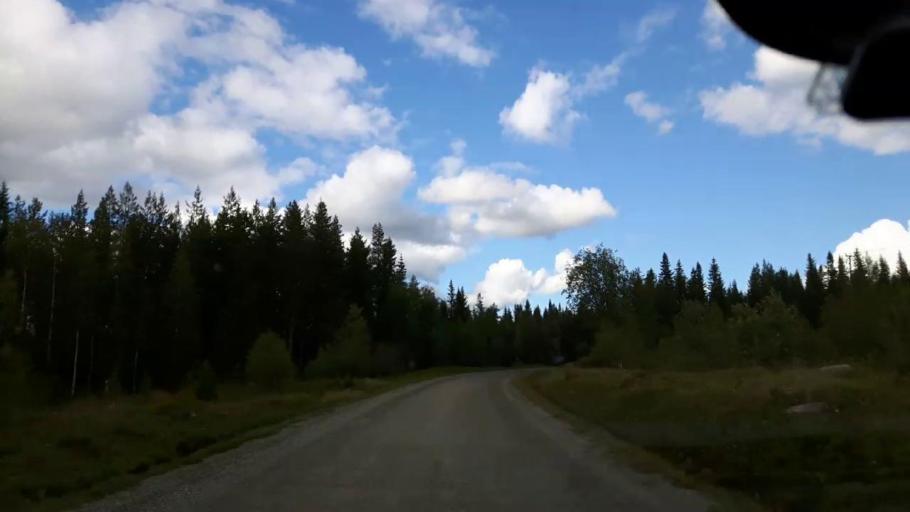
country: SE
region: Jaemtland
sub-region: Stroemsunds Kommun
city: Stroemsund
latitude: 63.4043
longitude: 15.7705
